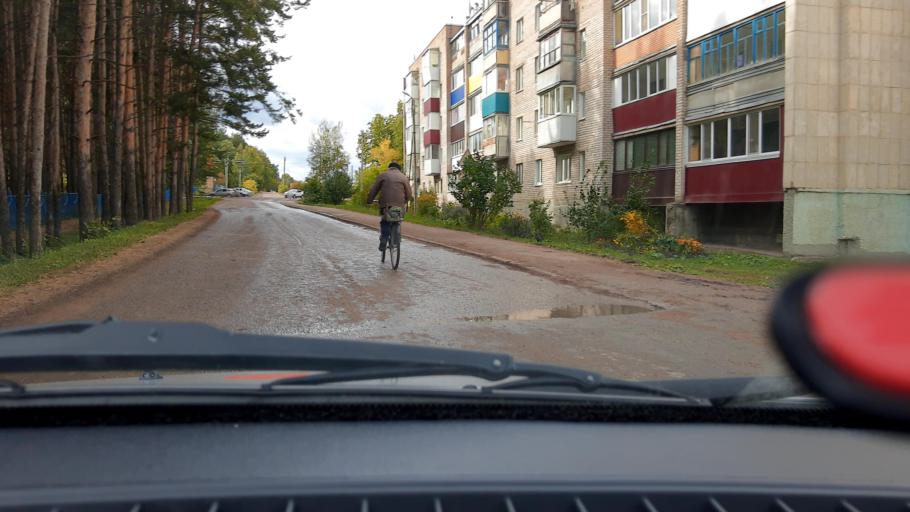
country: RU
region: Bashkortostan
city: Belebey
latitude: 54.1044
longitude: 54.0963
